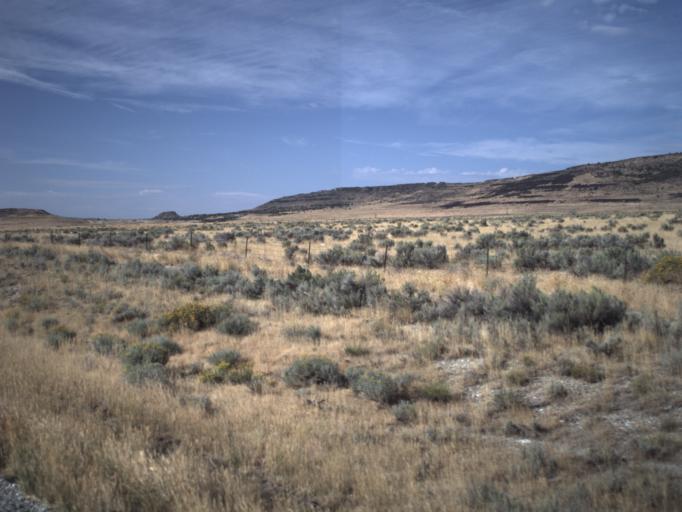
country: US
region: Idaho
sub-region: Minidoka County
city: Rupert
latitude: 41.8599
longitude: -113.1292
